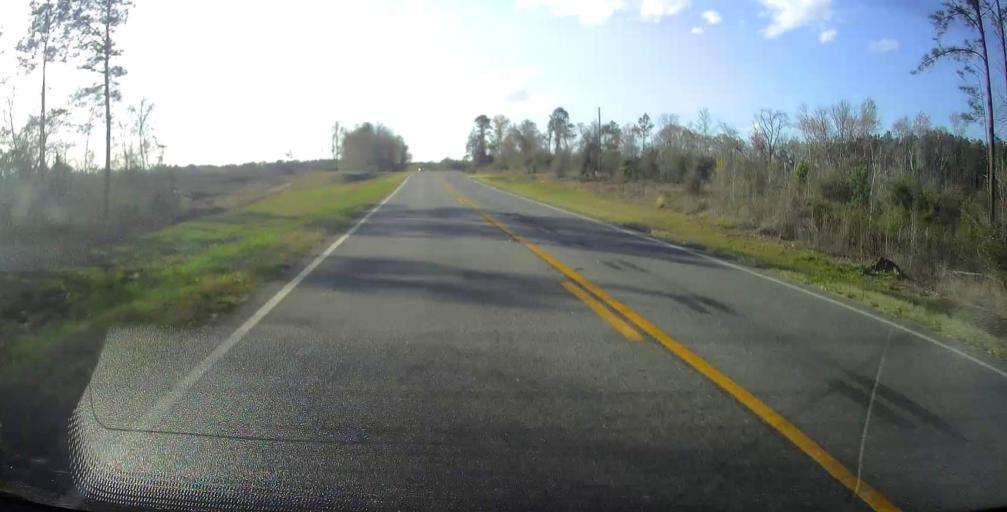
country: US
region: Georgia
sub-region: Tattnall County
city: Reidsville
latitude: 32.1313
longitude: -82.2191
